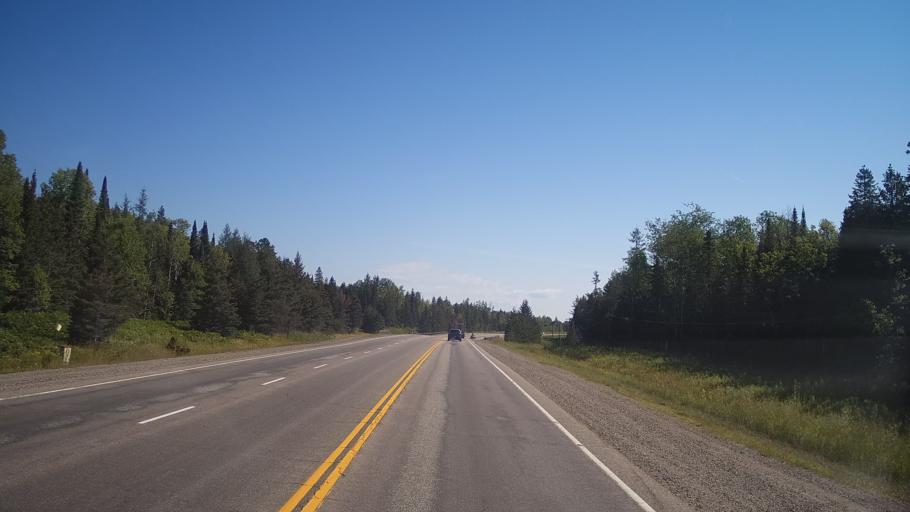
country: CA
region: Ontario
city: Espanola
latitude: 46.2475
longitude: -81.9290
